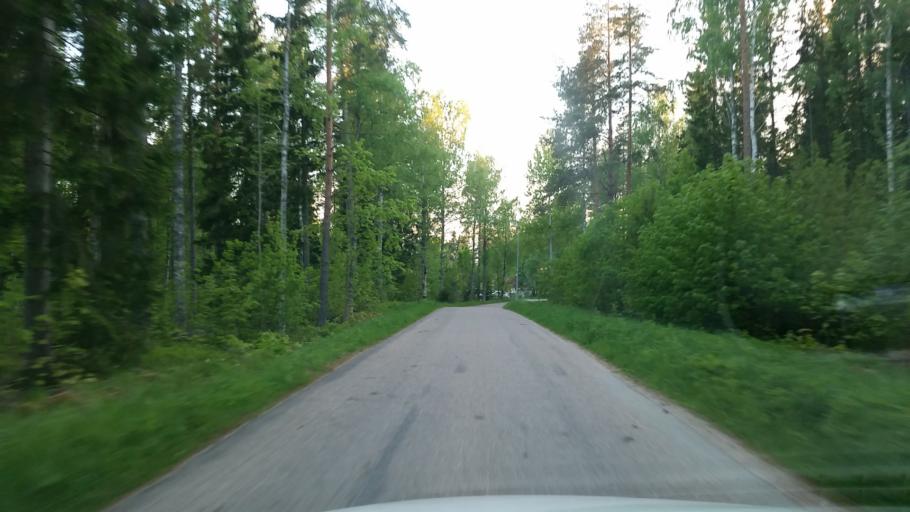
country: SE
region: Gaevleborg
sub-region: Gavle Kommun
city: Valbo
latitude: 60.6118
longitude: 16.9203
